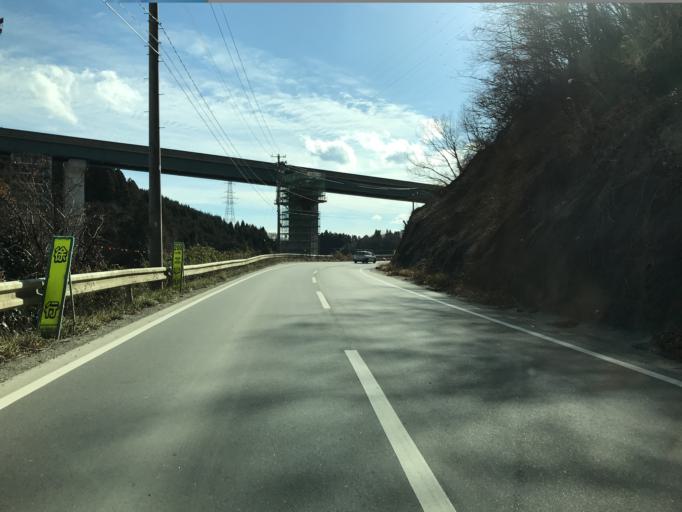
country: JP
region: Fukushima
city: Iwaki
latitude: 37.1076
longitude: 140.8808
